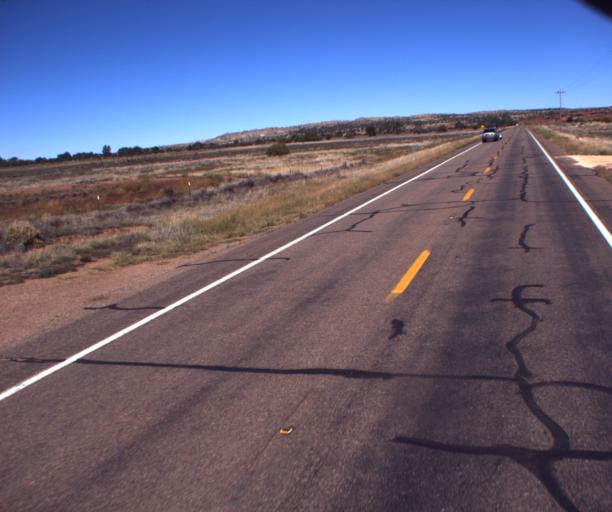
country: US
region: Arizona
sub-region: Apache County
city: Saint Johns
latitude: 34.4409
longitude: -109.4106
